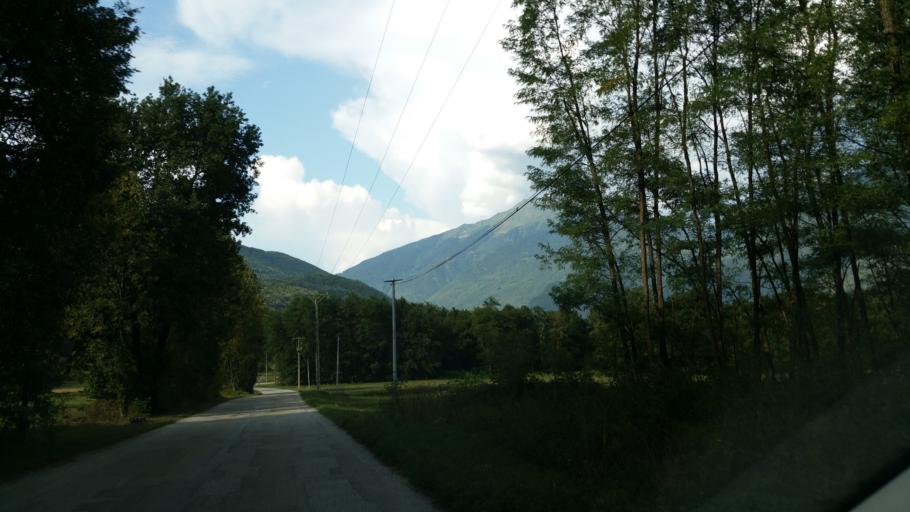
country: FR
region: Rhone-Alpes
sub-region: Departement de la Savoie
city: Saint-Remy-de-Maurienne
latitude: 45.4779
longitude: 6.2828
